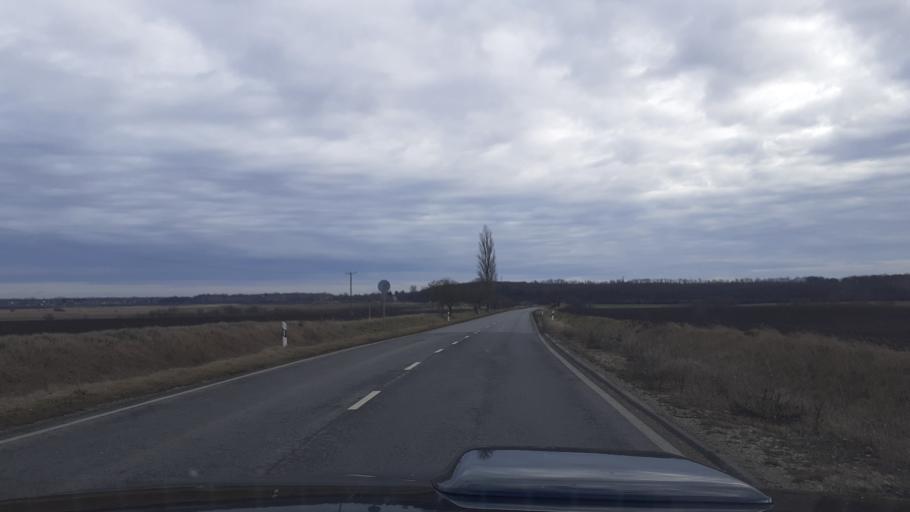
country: HU
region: Fejer
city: Seregelyes
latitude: 47.1287
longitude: 18.5487
